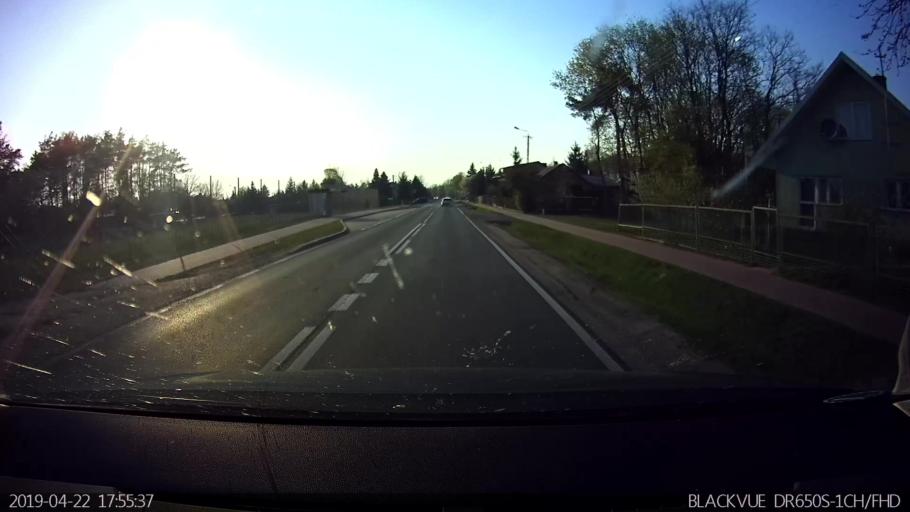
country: PL
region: Masovian Voivodeship
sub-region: Powiat wegrowski
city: Korytnica
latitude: 52.4622
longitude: 21.9168
